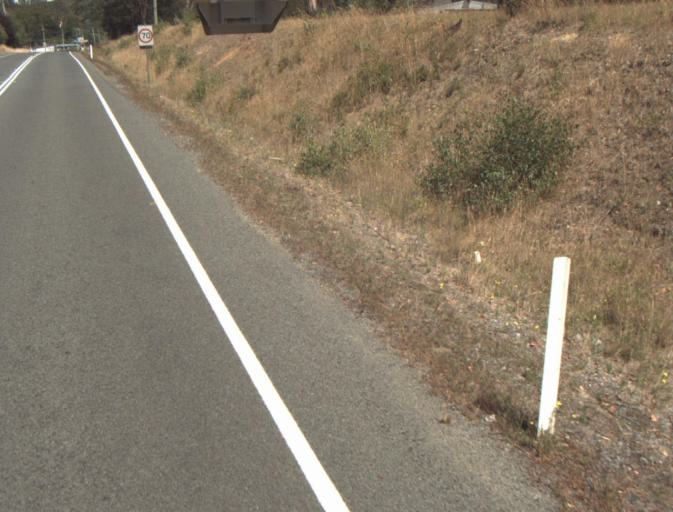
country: AU
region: Tasmania
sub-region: Launceston
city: Newstead
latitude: -41.3866
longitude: 147.3067
